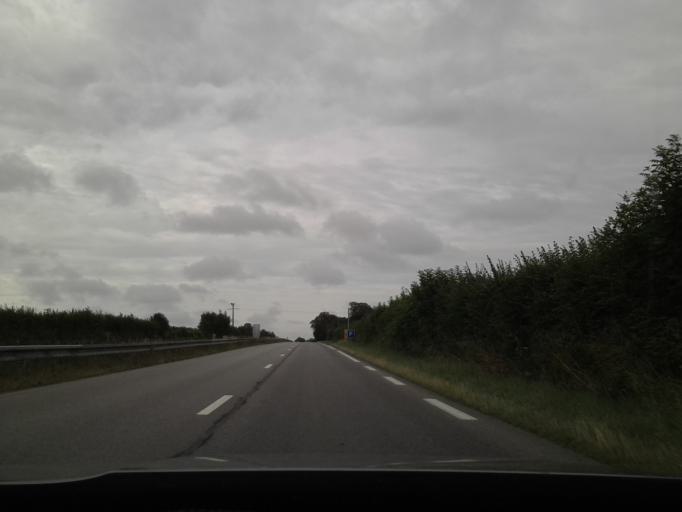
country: FR
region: Lower Normandy
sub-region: Departement de la Manche
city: Carentan
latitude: 49.3553
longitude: -1.2779
